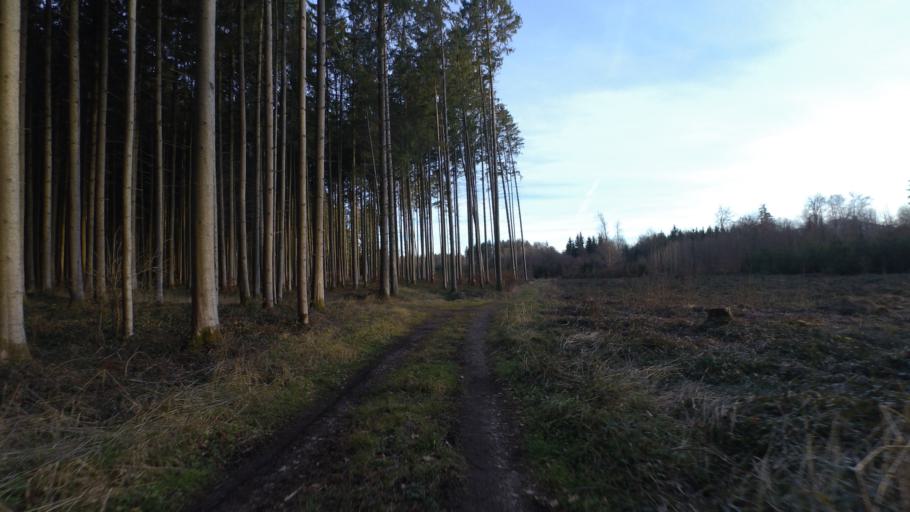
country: DE
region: Bavaria
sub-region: Upper Bavaria
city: Chieming
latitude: 47.8755
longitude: 12.5495
